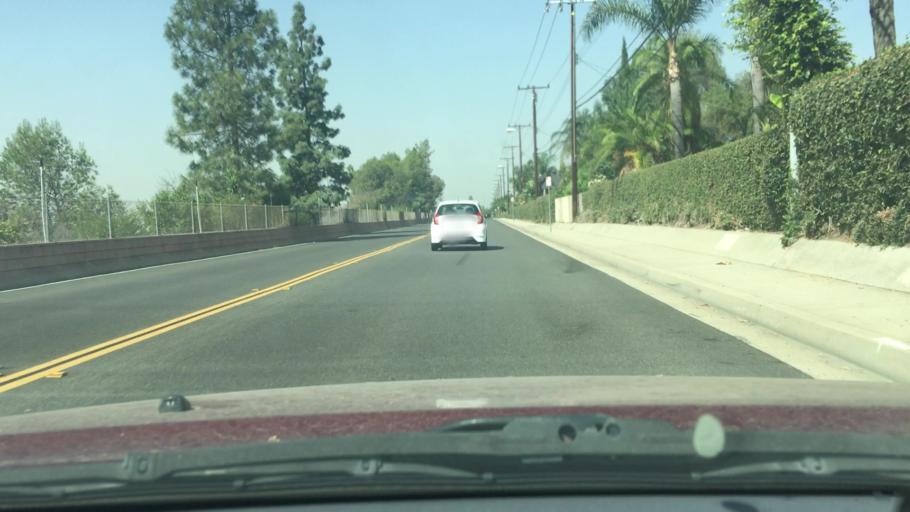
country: US
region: California
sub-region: Orange County
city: Buena Park
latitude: 33.8896
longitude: -118.0144
